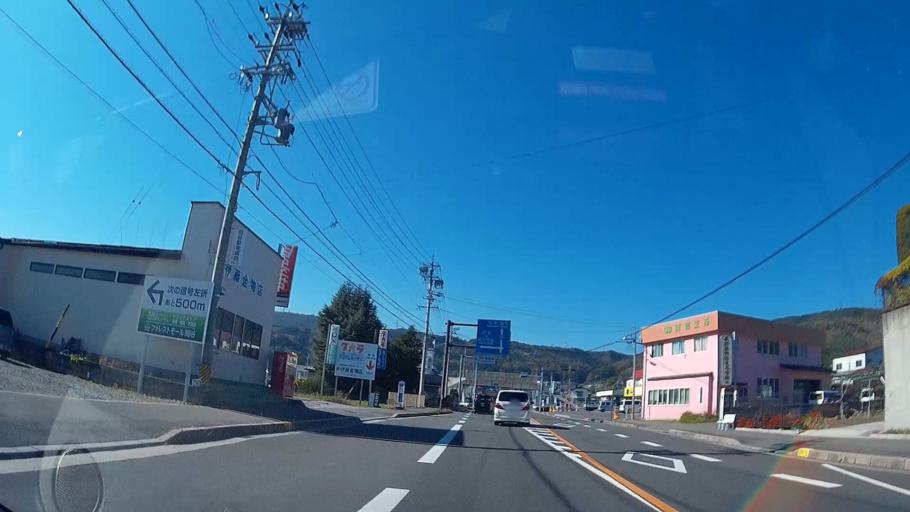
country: JP
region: Nagano
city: Okaya
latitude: 36.0820
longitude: 138.0482
